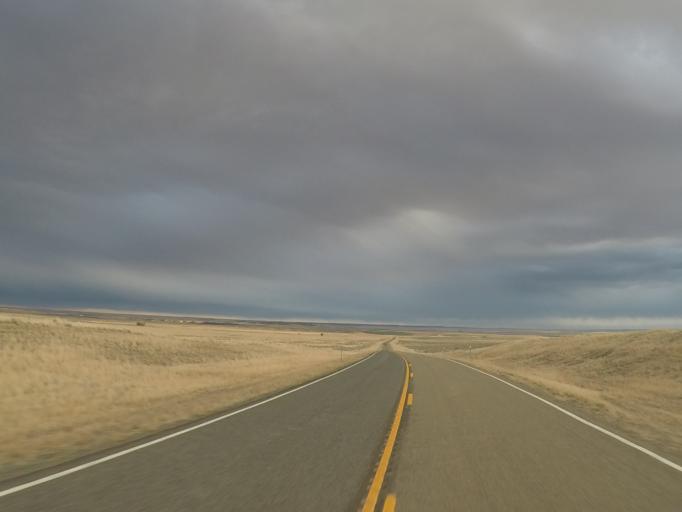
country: US
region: Montana
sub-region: Golden Valley County
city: Ryegate
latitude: 46.4117
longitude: -109.2573
